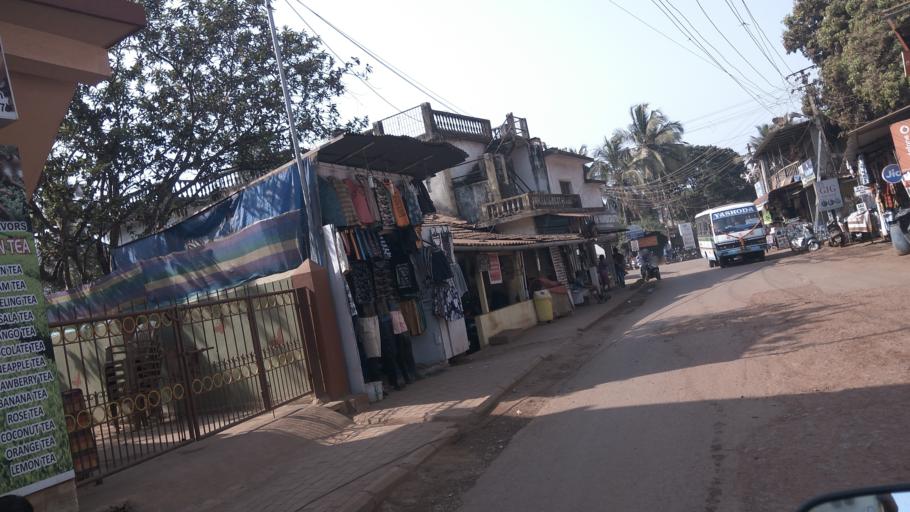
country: IN
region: Goa
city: Calangute
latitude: 15.5607
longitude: 73.7533
